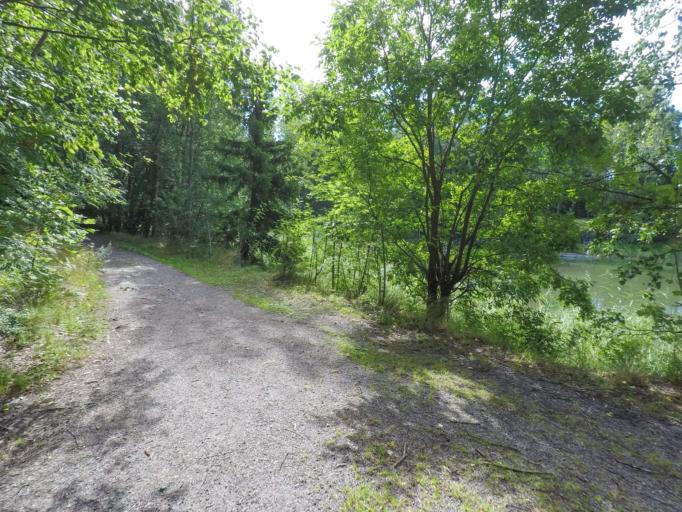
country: FI
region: Uusimaa
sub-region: Helsinki
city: Vantaa
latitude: 60.1662
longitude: 25.0703
